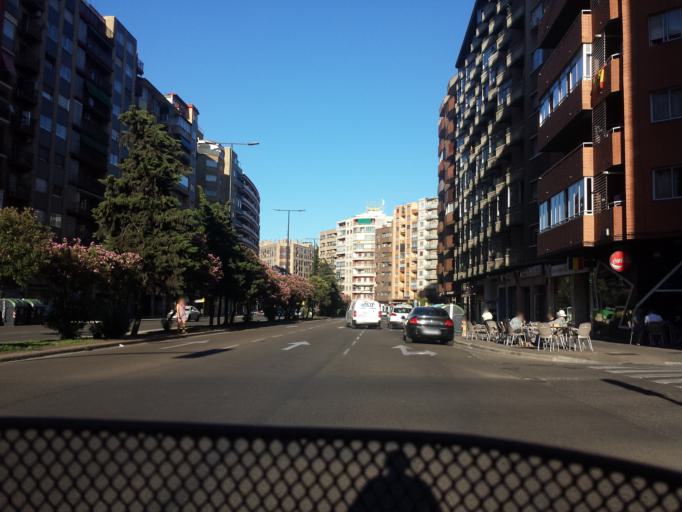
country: ES
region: Aragon
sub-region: Provincia de Zaragoza
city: Almozara
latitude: 41.6548
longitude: -0.9026
